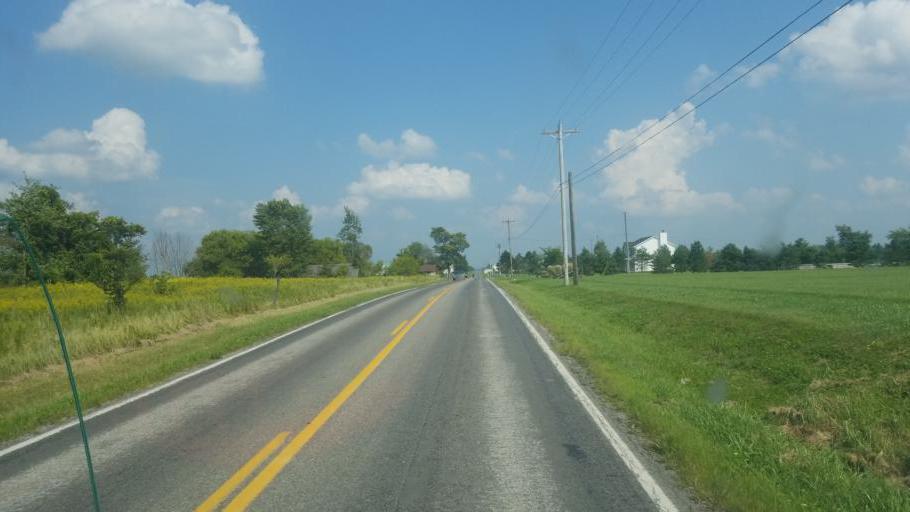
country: US
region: Ohio
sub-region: Wayne County
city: West Salem
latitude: 41.0566
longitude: -82.1654
